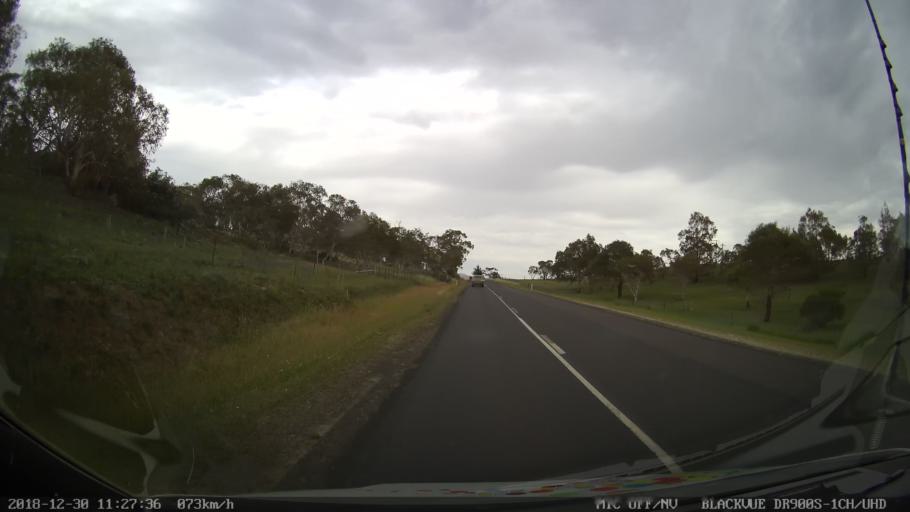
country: AU
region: New South Wales
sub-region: Snowy River
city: Jindabyne
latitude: -36.4591
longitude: 148.6255
